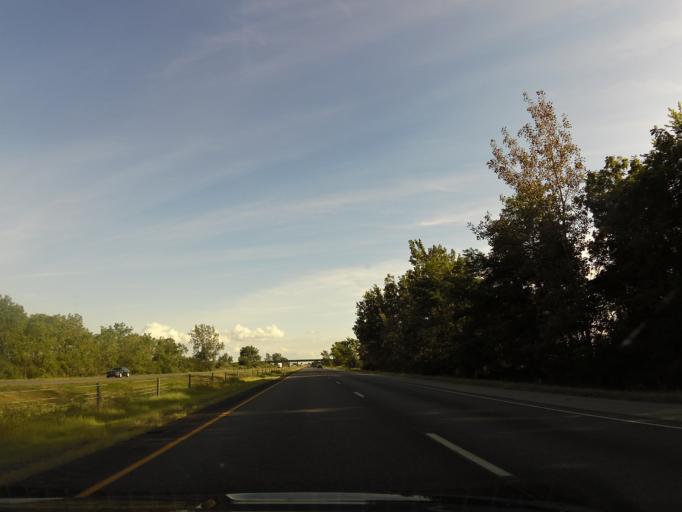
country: US
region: Indiana
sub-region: Jasper County
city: Remington
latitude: 40.8413
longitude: -87.1747
